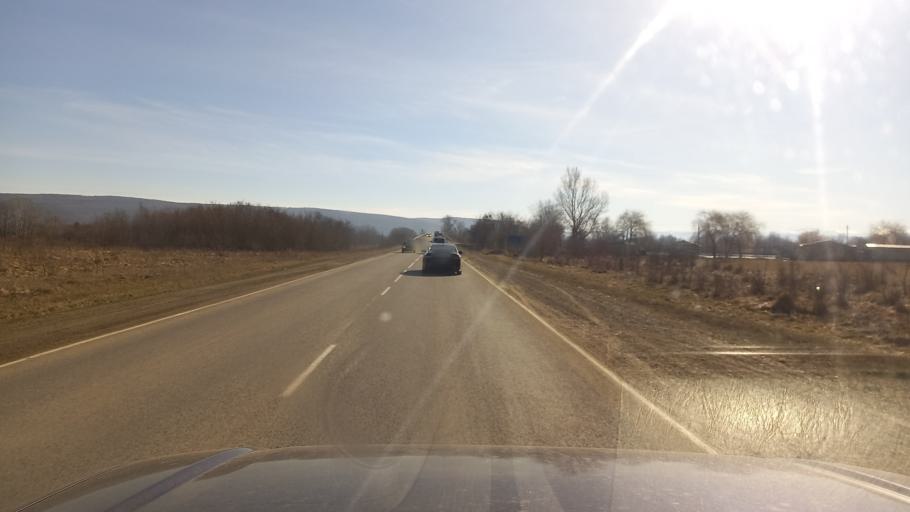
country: RU
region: Adygeya
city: Tul'skiy
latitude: 44.5165
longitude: 40.1429
